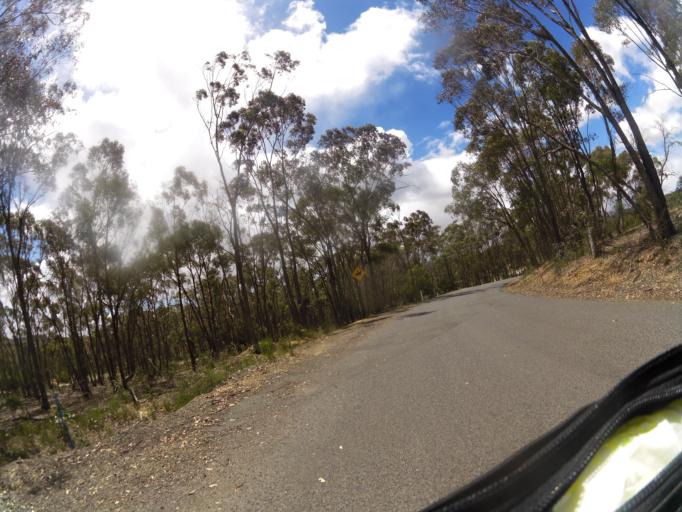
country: AU
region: Victoria
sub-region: Mount Alexander
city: Castlemaine
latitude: -37.0205
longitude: 144.2452
